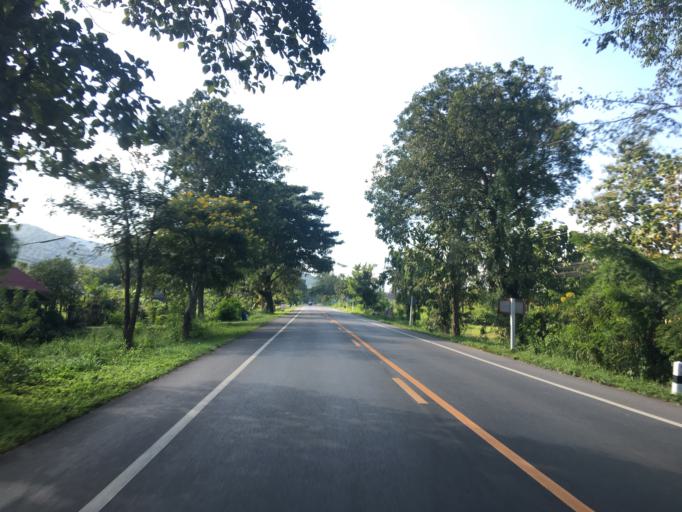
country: TH
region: Phayao
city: Chun
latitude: 19.3496
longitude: 100.1107
